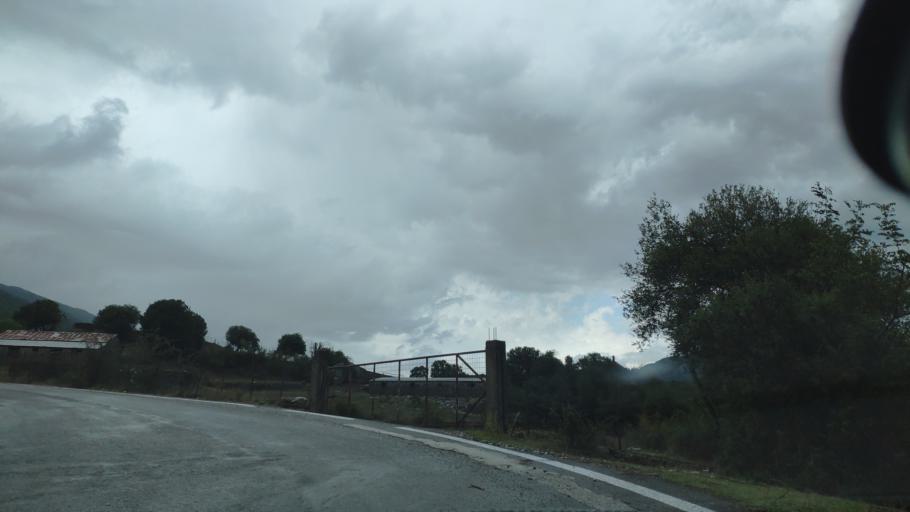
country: GR
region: Central Greece
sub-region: Nomos Evrytanias
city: Kerasochori
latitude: 39.1058
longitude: 21.4230
